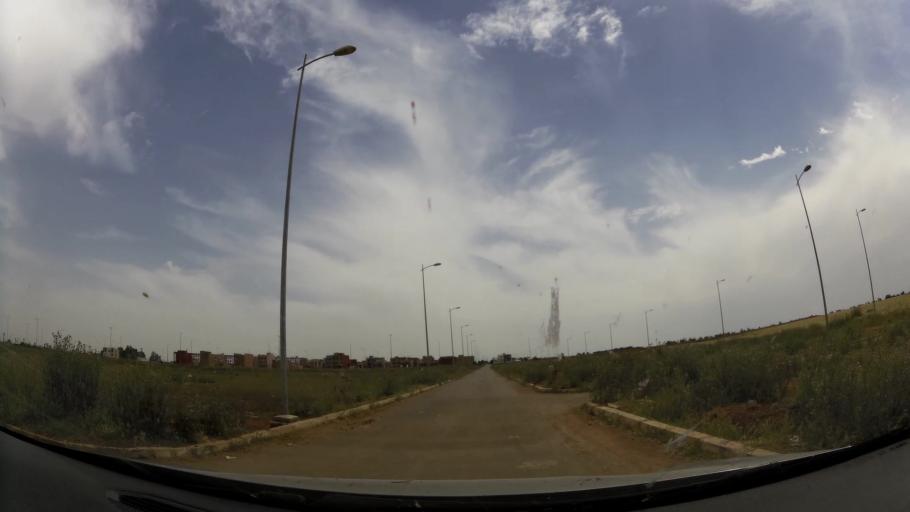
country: MA
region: Rabat-Sale-Zemmour-Zaer
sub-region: Khemisset
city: Khemisset
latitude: 33.8190
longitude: -6.0923
